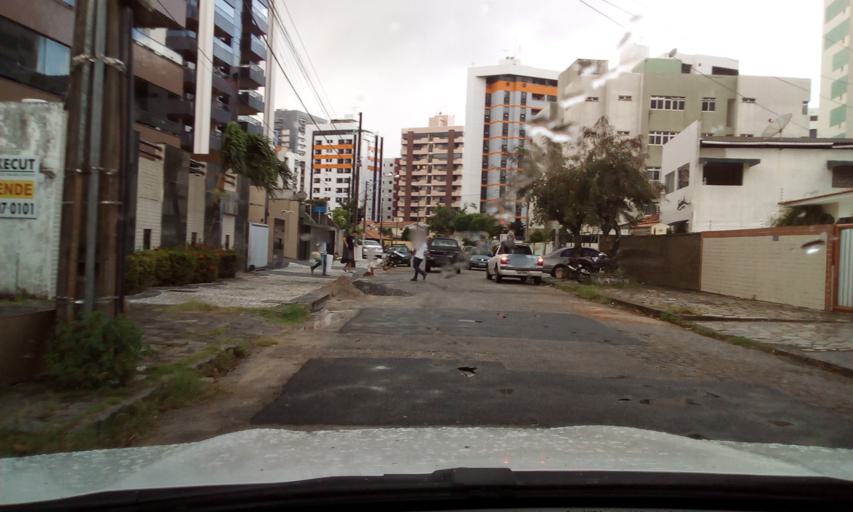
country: BR
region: Paraiba
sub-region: Joao Pessoa
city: Joao Pessoa
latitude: -7.1001
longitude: -34.8359
